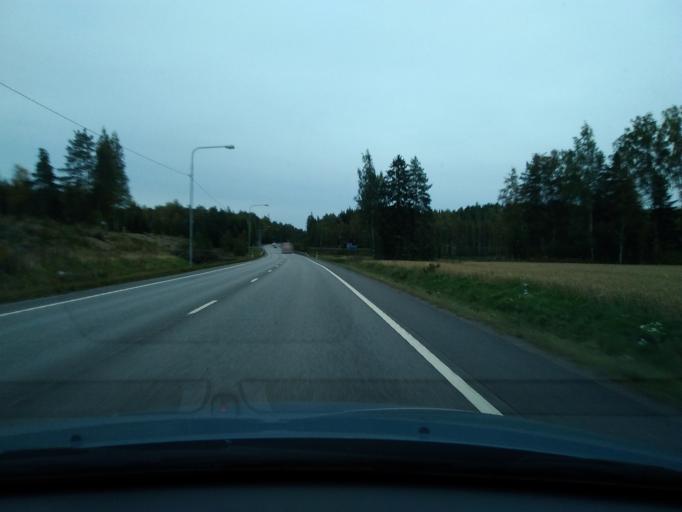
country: FI
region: Uusimaa
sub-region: Helsinki
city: Maentsaelae
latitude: 60.6176
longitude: 25.3248
